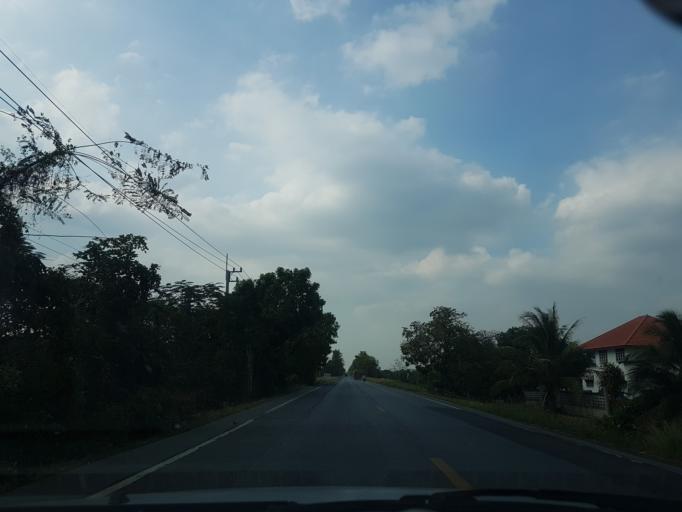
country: TH
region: Phra Nakhon Si Ayutthaya
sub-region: Amphoe Tha Ruea
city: Tha Ruea
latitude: 14.5377
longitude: 100.7428
